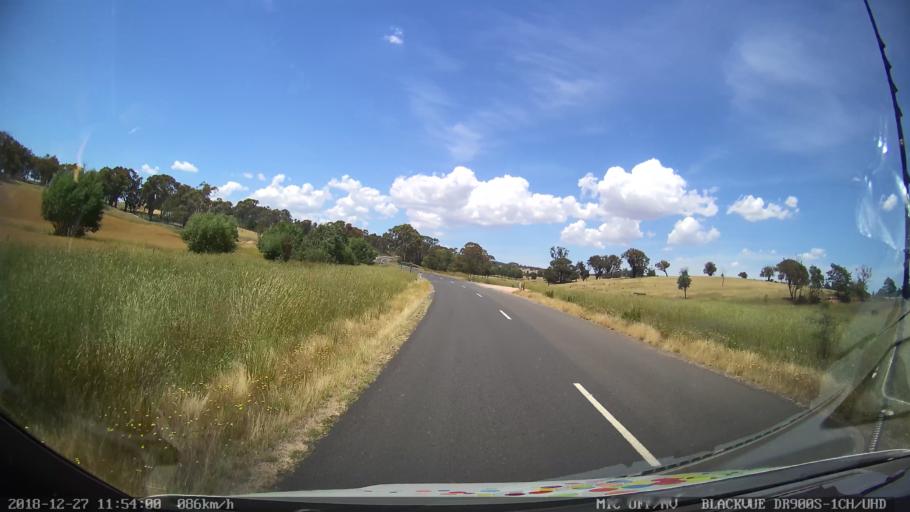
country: AU
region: New South Wales
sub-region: Blayney
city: Blayney
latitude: -33.6693
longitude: 149.4019
